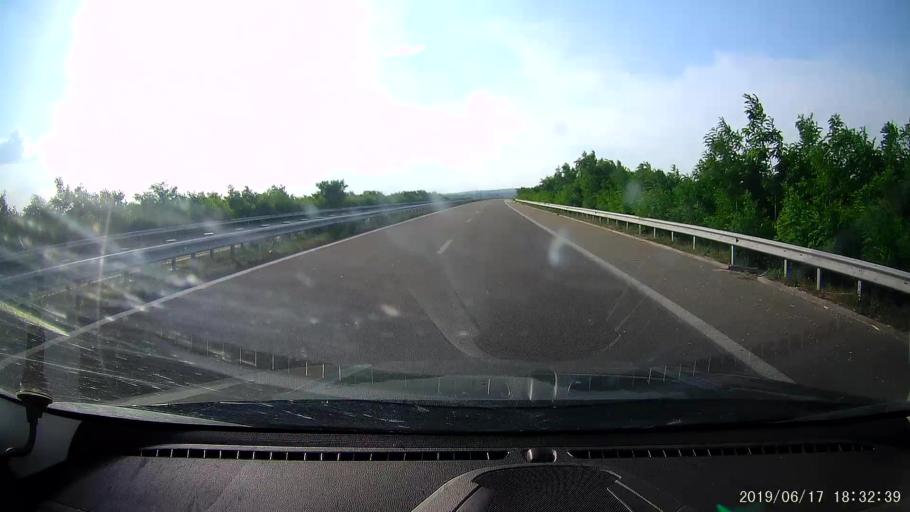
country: BG
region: Khaskovo
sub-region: Obshtina Dimitrovgrad
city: Dimitrovgrad
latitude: 42.0636
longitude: 25.4738
